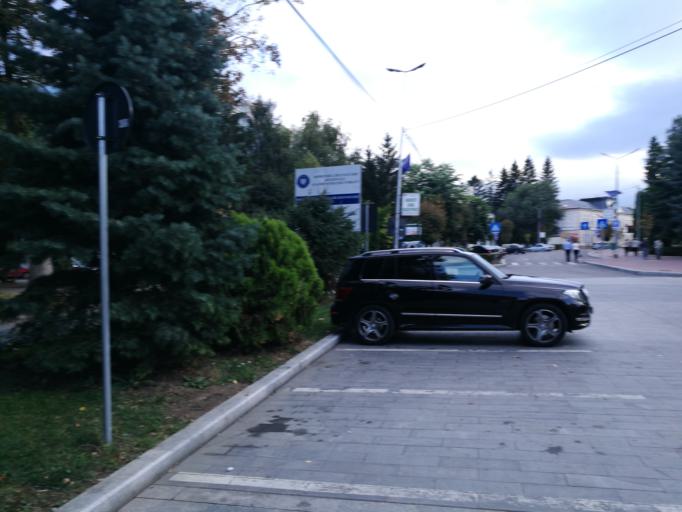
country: RO
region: Suceava
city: Suceava
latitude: 47.6427
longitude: 26.2588
